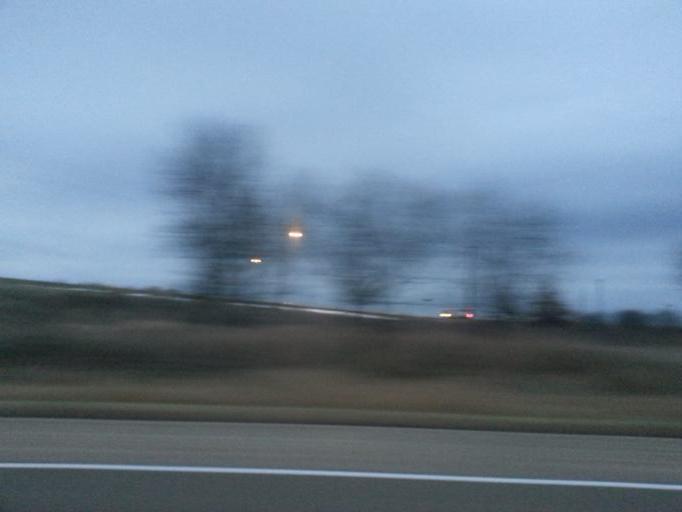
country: US
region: Iowa
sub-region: Black Hawk County
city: La Porte City
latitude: 42.4127
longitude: -92.1707
